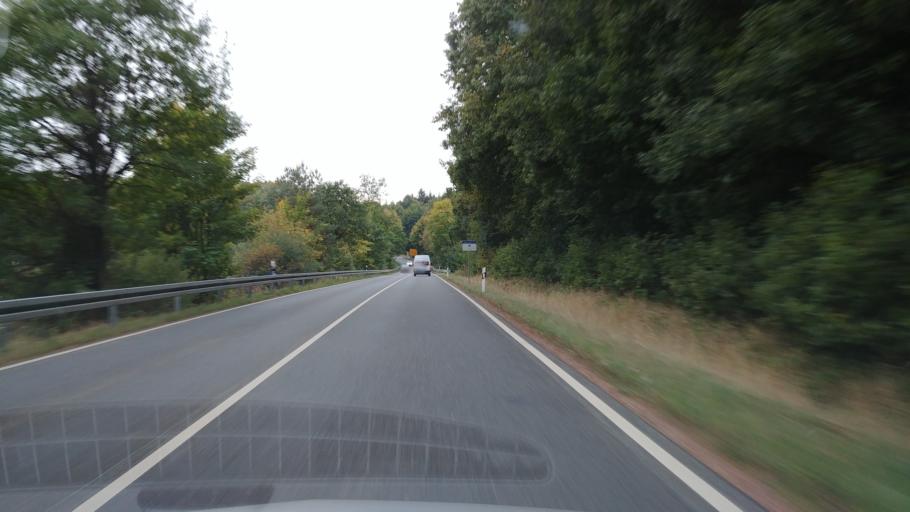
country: DE
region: Rheinland-Pfalz
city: Kaltenholzhausen
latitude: 50.2754
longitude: 8.1680
